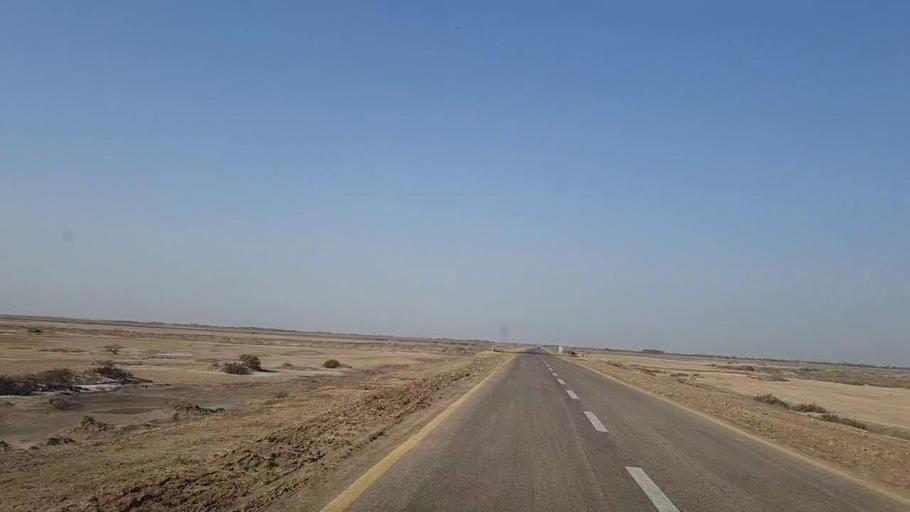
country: PK
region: Sindh
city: Jati
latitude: 24.4934
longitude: 68.3758
